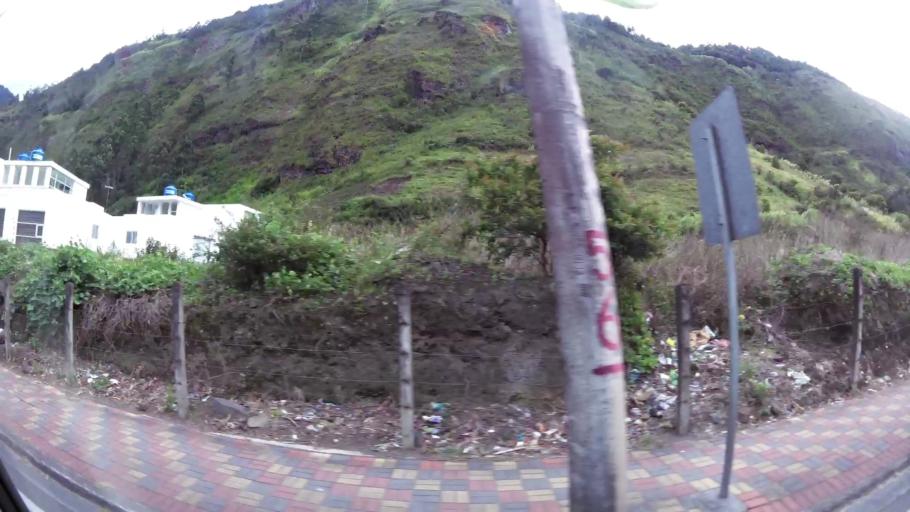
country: EC
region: Tungurahua
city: Banos
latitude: -1.3948
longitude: -78.4103
